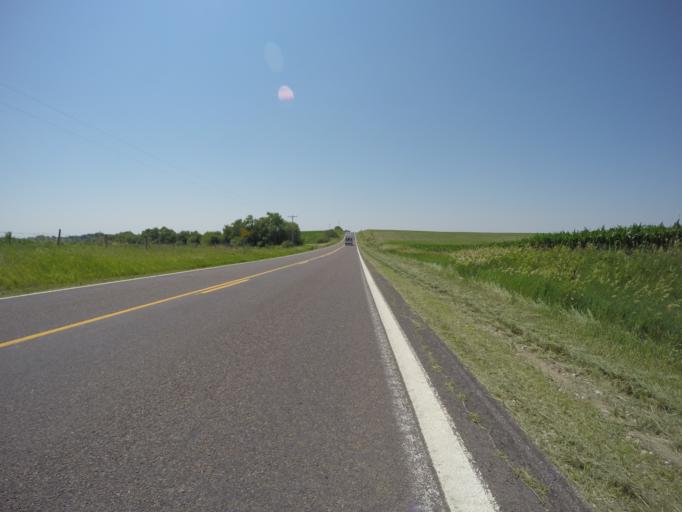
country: US
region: Kansas
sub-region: Doniphan County
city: Highland
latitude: 39.8315
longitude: -95.2653
